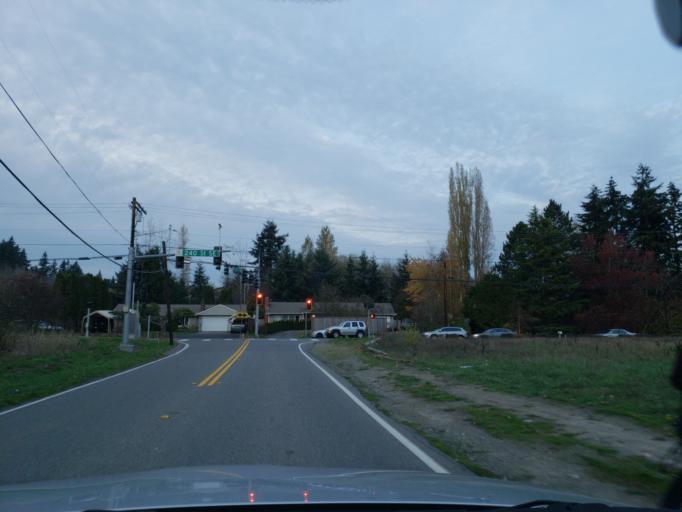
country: US
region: Washington
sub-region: King County
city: Bothell
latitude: 47.7798
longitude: -122.2232
